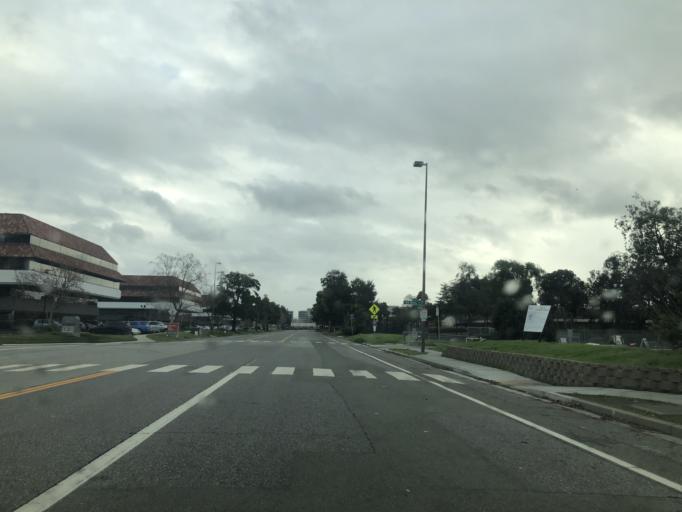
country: US
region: California
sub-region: Santa Clara County
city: Santa Clara
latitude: 37.4001
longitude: -121.9796
